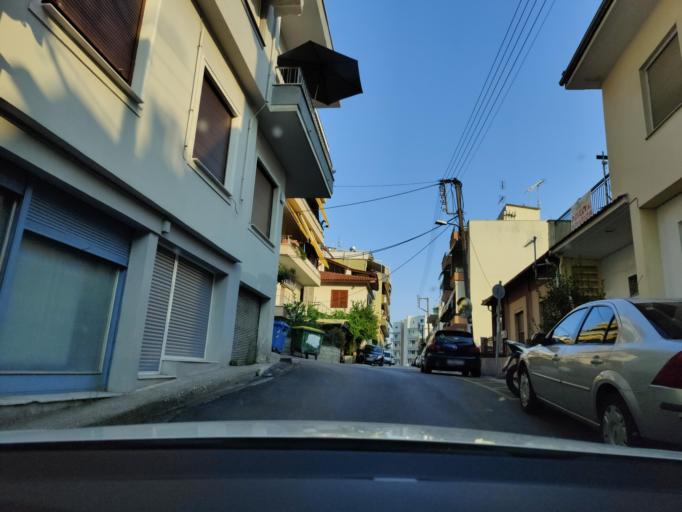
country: GR
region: East Macedonia and Thrace
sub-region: Nomos Kavalas
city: Kavala
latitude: 40.9394
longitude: 24.3980
